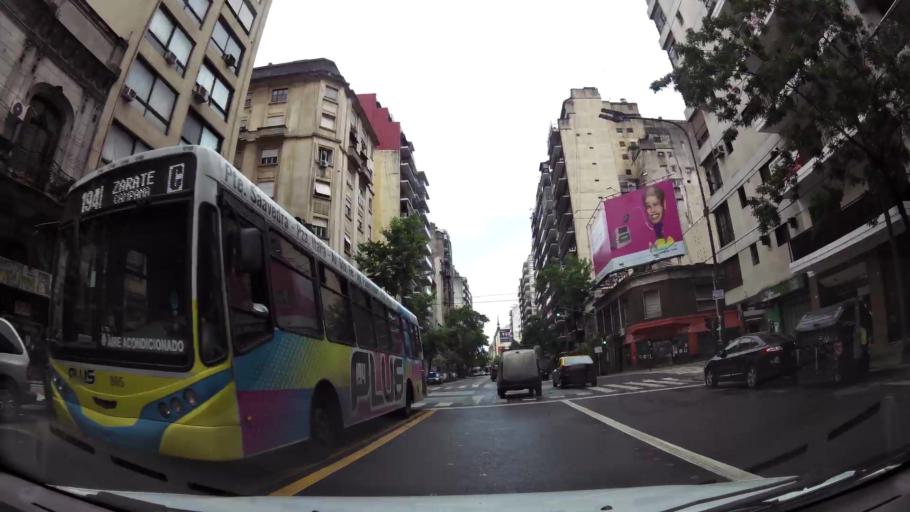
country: AR
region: Buenos Aires F.D.
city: Retiro
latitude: -34.5998
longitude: -58.4042
